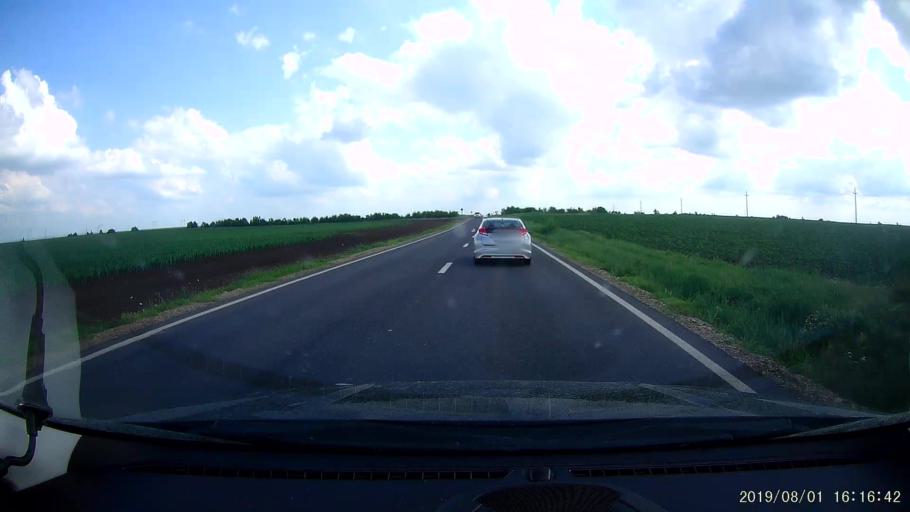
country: RO
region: Calarasi
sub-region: Comuna Stefan Voda
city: Stefan Voda
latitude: 44.3157
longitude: 27.3572
